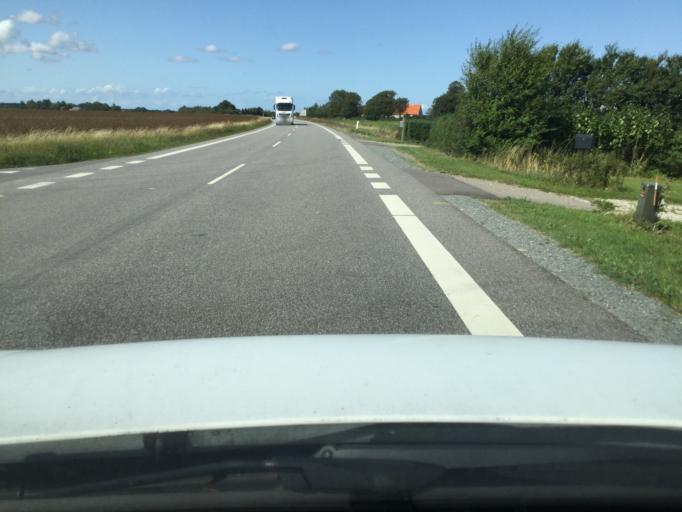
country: DK
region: Zealand
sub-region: Lolland Kommune
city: Rodby
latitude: 54.7428
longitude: 11.3886
